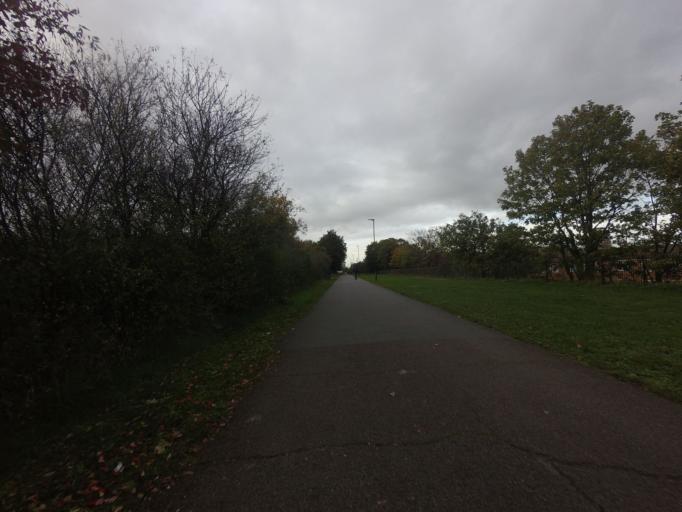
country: GB
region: England
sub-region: Greater London
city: East Ham
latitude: 51.5270
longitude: 0.0195
